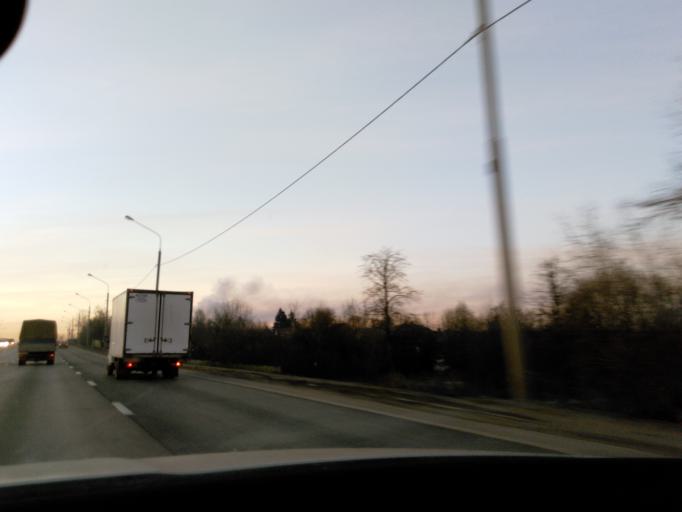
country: RU
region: Moskovskaya
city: Novopodrezkovo
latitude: 55.9285
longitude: 37.3817
